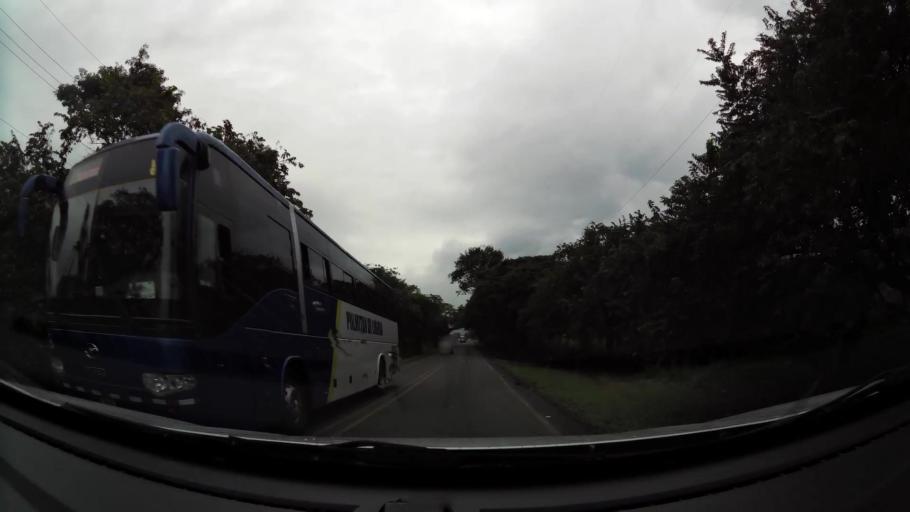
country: CR
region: Puntarenas
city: Esparza
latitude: 9.9941
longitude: -84.7095
